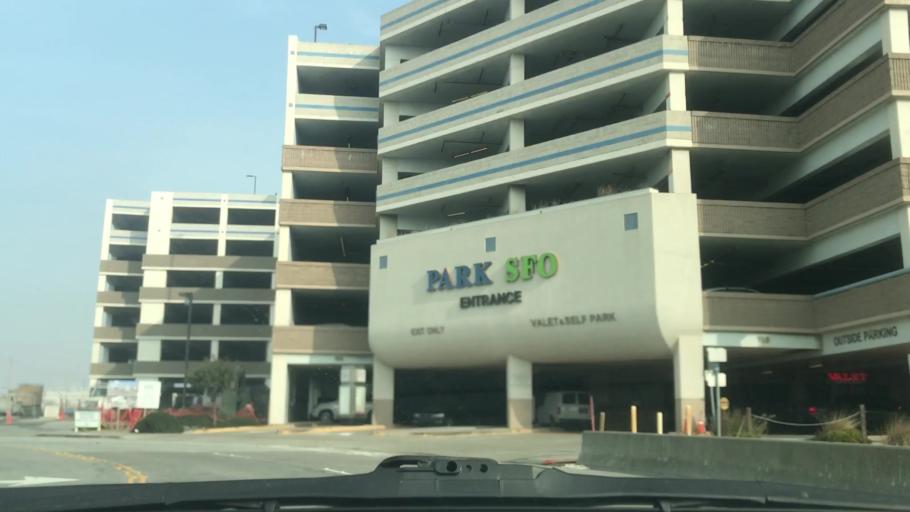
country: US
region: California
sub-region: San Mateo County
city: San Bruno
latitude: 37.6389
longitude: -122.3977
